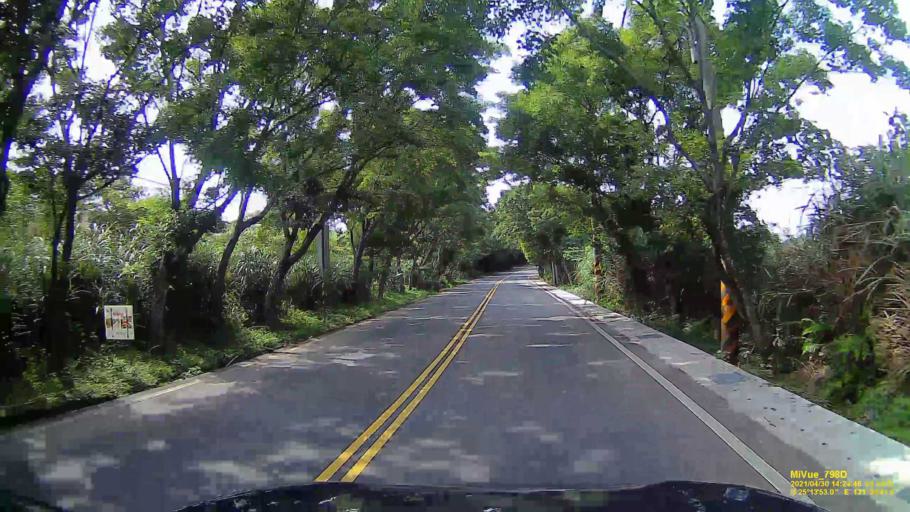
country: TW
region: Taipei
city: Taipei
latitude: 25.2317
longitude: 121.5113
